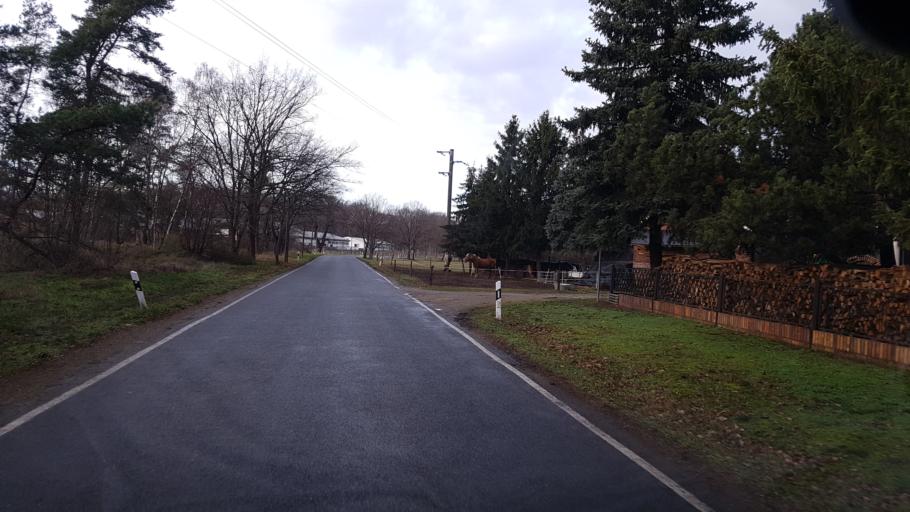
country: DE
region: Brandenburg
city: Altdobern
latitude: 51.6675
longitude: 13.9893
